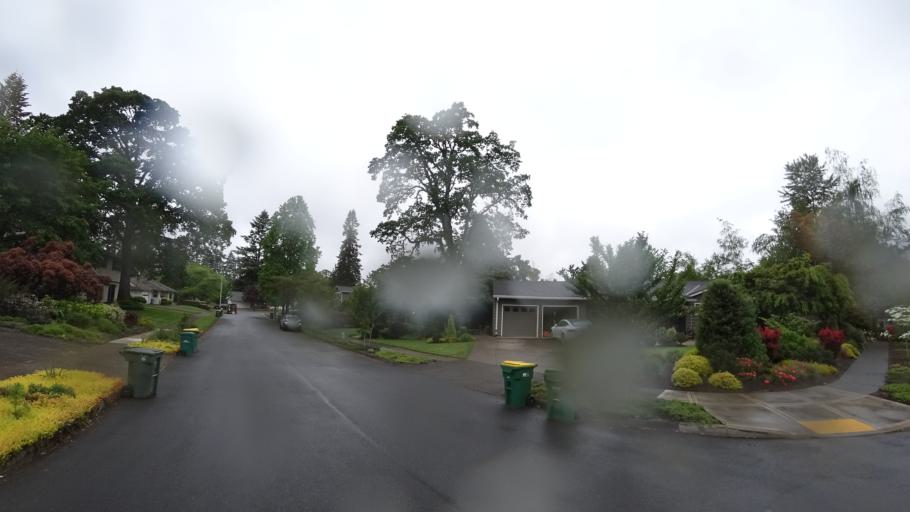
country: US
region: Oregon
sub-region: Washington County
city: Raleigh Hills
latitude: 45.4786
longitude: -122.7725
